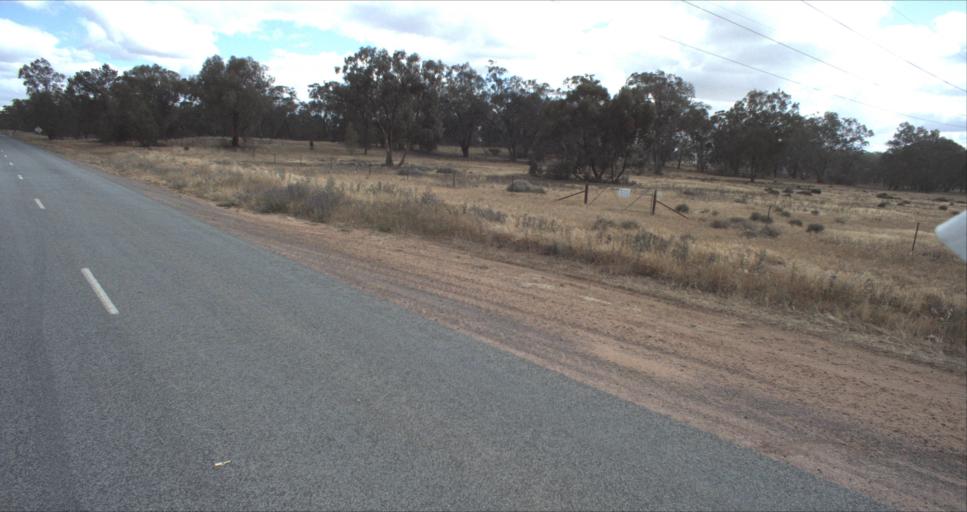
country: AU
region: New South Wales
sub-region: Leeton
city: Leeton
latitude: -34.6439
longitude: 146.3525
